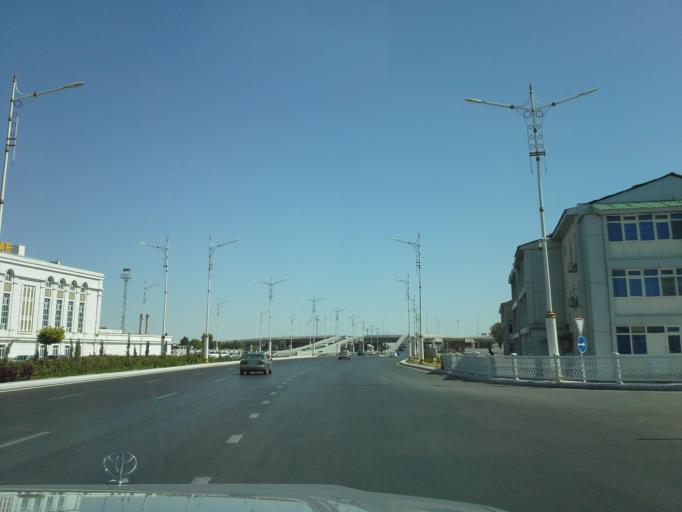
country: TM
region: Ahal
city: Ashgabat
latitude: 37.9421
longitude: 58.3963
